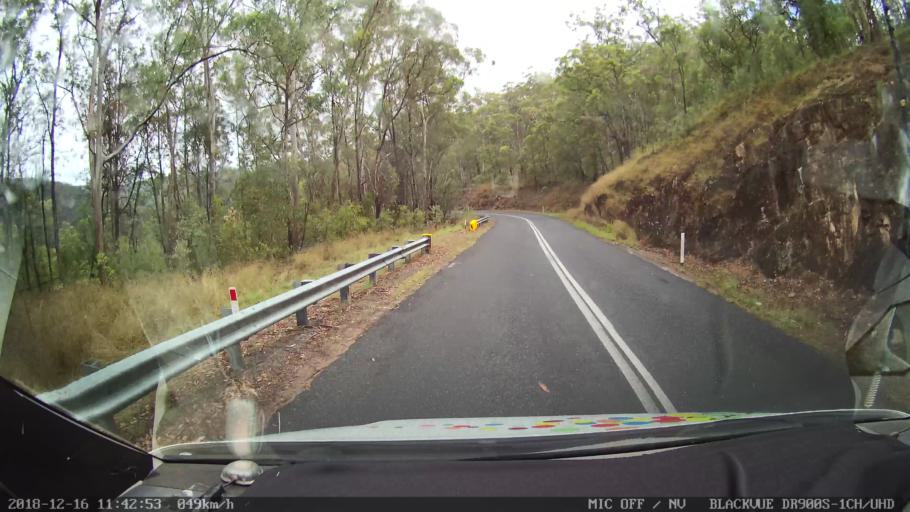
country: AU
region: New South Wales
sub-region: Tenterfield Municipality
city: Carrolls Creek
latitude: -28.9496
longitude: 152.2152
